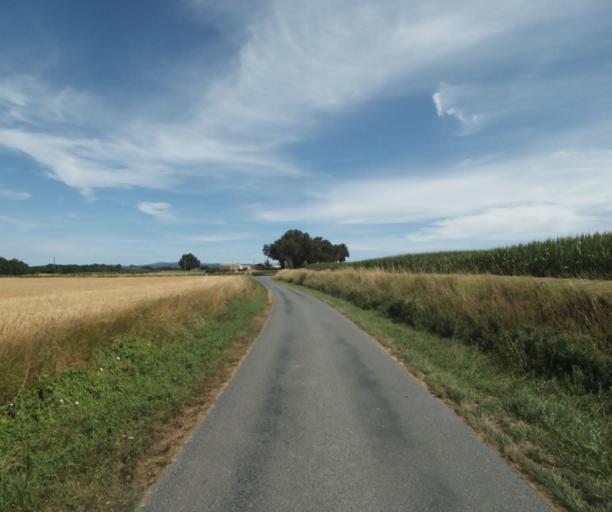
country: FR
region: Midi-Pyrenees
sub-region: Departement de la Haute-Garonne
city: Revel
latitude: 43.5125
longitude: 2.0412
